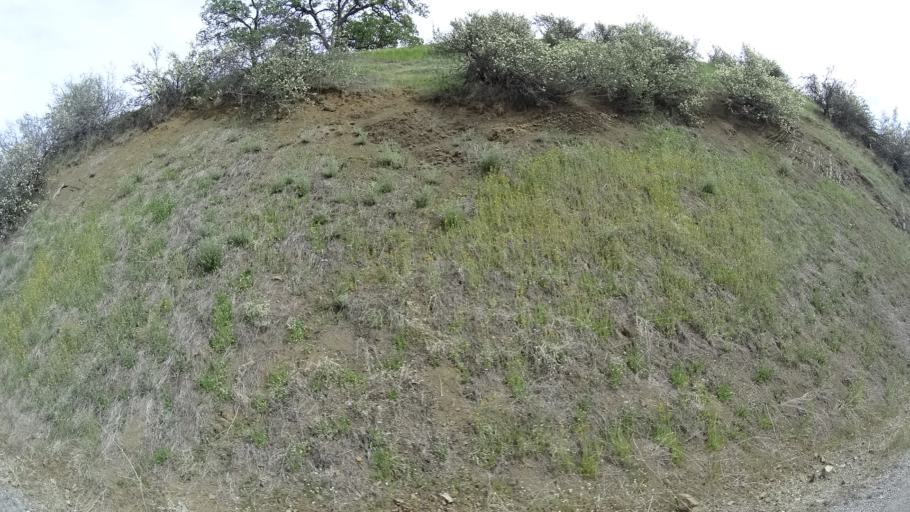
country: US
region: California
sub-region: Glenn County
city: Willows
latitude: 39.6193
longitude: -122.5921
